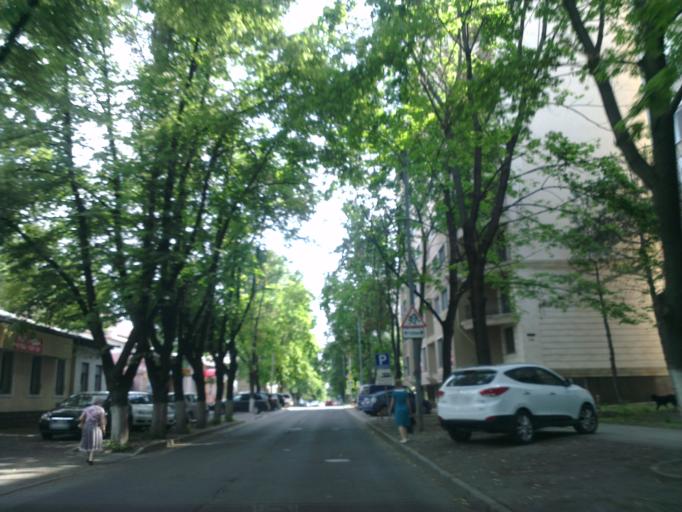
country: MD
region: Chisinau
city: Chisinau
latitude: 47.0278
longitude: 28.8228
